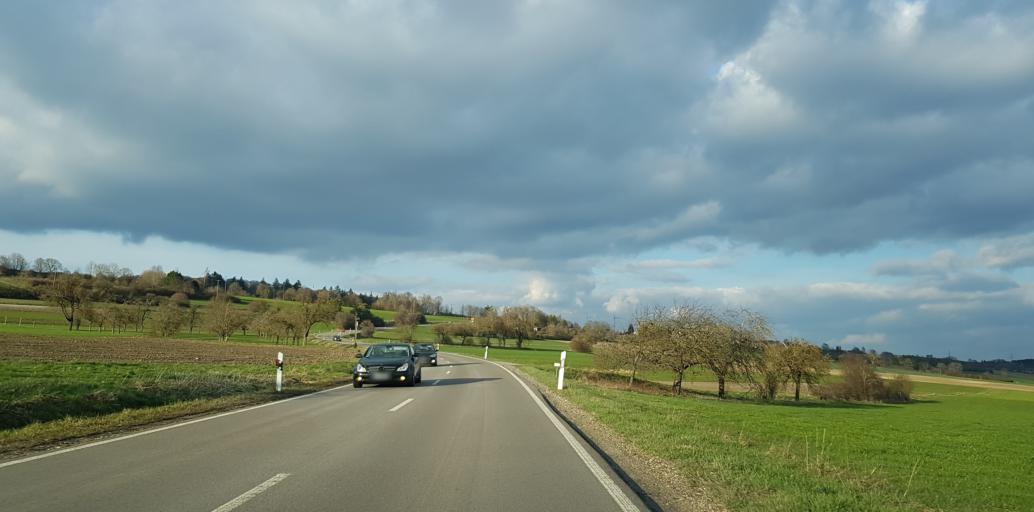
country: DE
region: Baden-Wuerttemberg
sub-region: Tuebingen Region
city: Erbach
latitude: 48.3706
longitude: 9.8811
